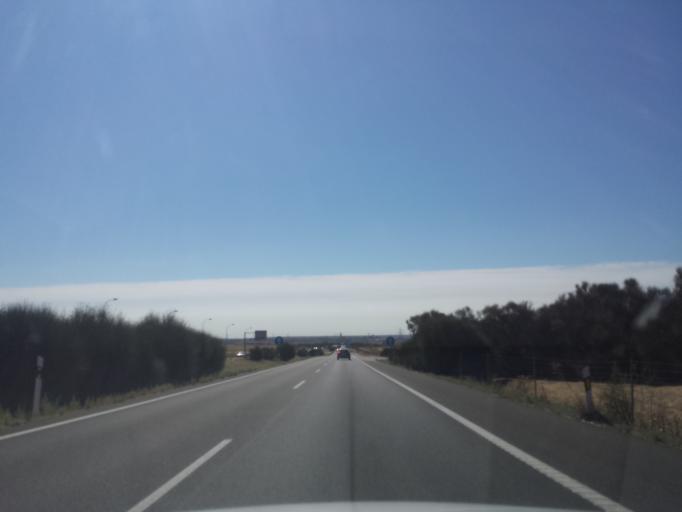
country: ES
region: Castille and Leon
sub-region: Provincia de Valladolid
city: Bercero
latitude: 41.5241
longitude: -5.0424
